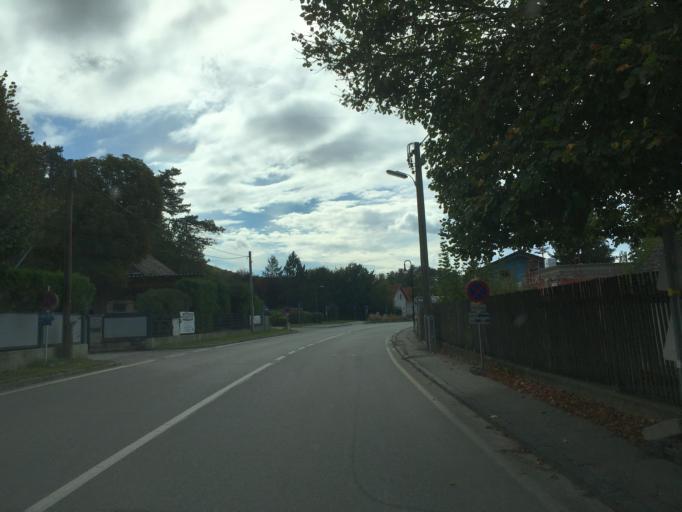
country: AT
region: Lower Austria
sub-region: Politischer Bezirk Modling
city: Gaaden
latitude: 48.0622
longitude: 16.2160
